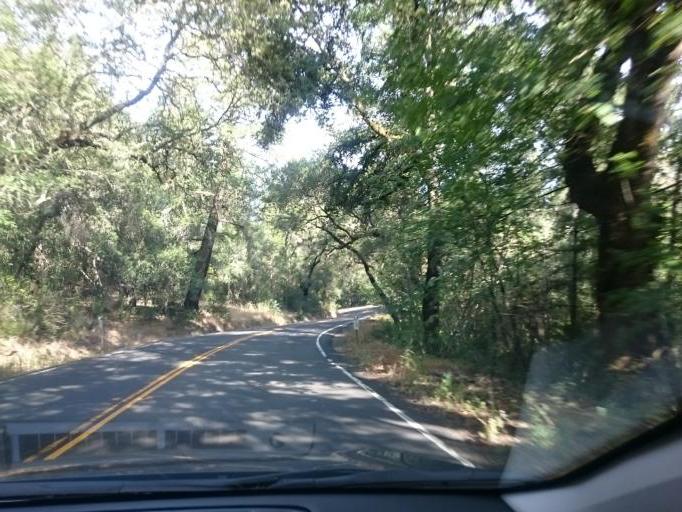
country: US
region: California
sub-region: Napa County
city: Calistoga
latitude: 38.6015
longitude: -122.6372
